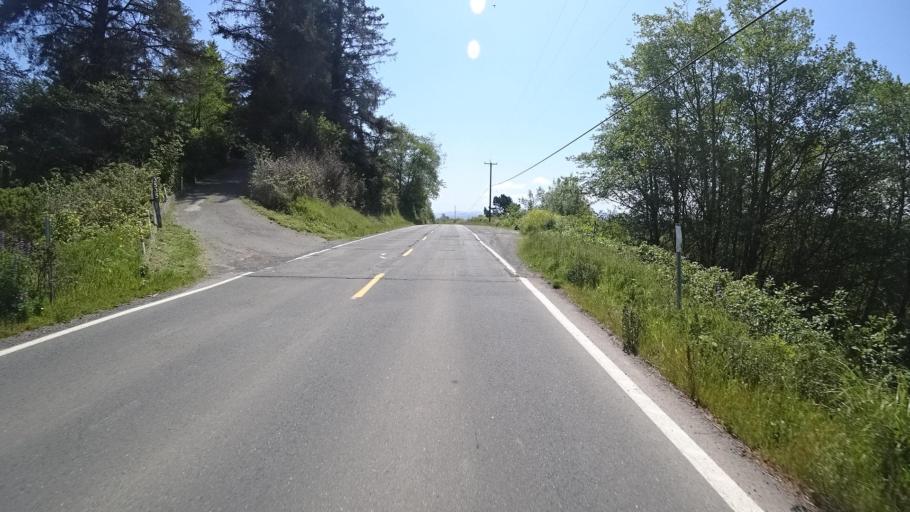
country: US
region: California
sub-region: Humboldt County
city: Ferndale
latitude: 40.6307
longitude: -124.2218
